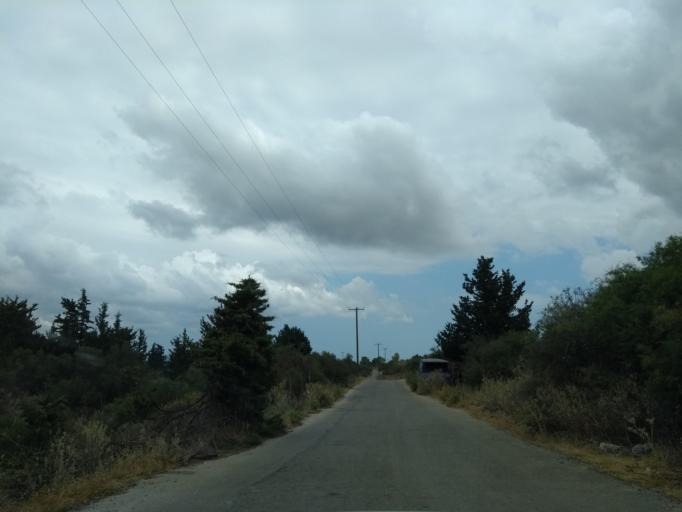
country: GR
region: Crete
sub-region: Nomos Chanias
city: Georgioupolis
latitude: 35.3983
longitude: 24.2277
